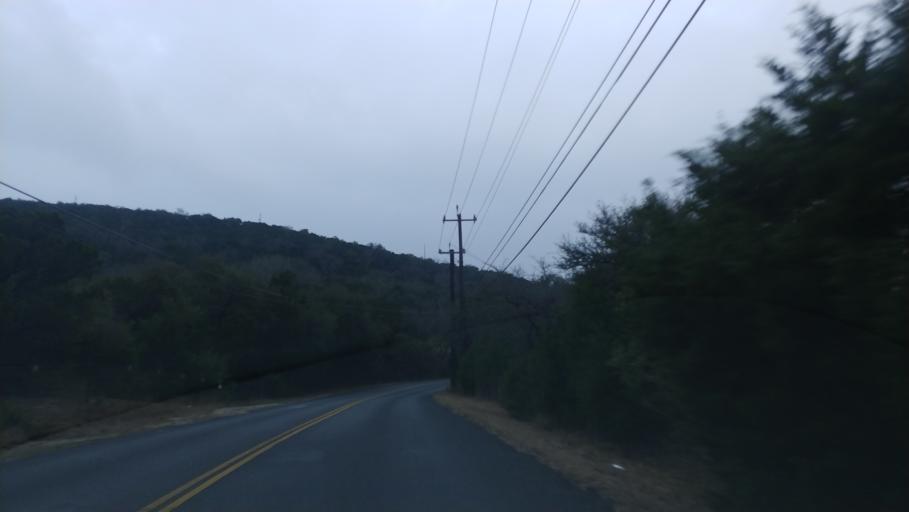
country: US
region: Texas
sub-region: Bexar County
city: Cross Mountain
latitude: 29.6356
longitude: -98.6786
